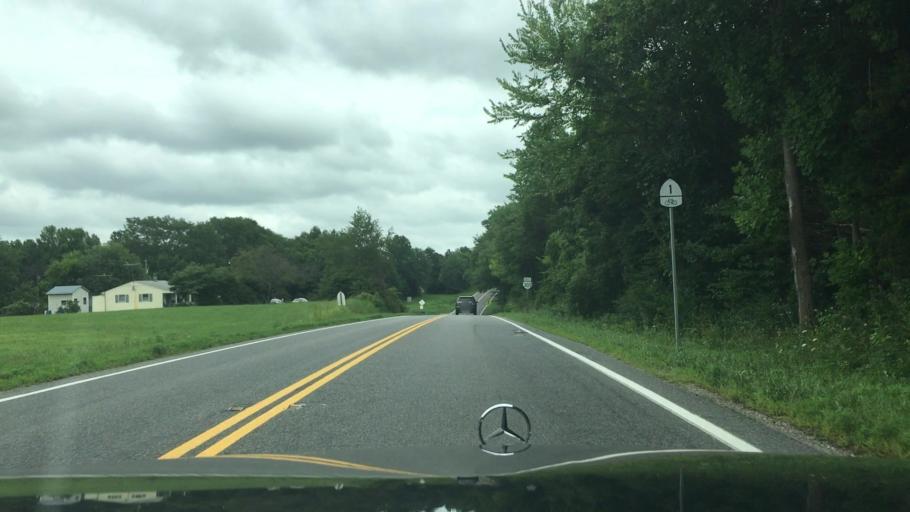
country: US
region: Virginia
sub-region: Nottoway County
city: Crewe
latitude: 37.2802
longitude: -78.2041
